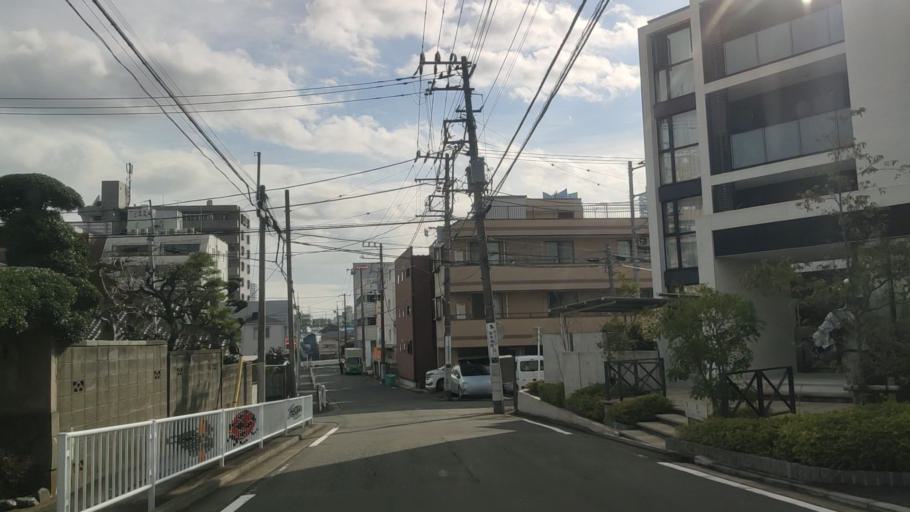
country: JP
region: Kanagawa
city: Yokohama
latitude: 35.4740
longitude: 139.6268
